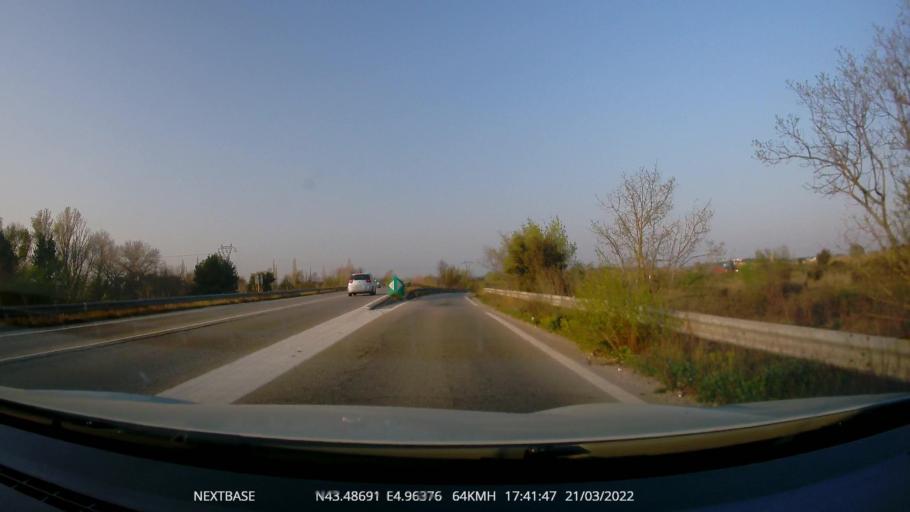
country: FR
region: Provence-Alpes-Cote d'Azur
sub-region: Departement des Bouches-du-Rhone
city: Istres
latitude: 43.4871
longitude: 4.9638
